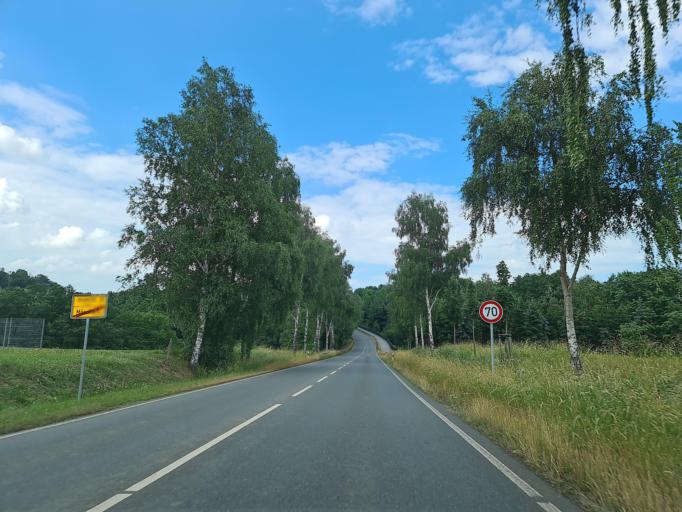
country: DE
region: Saxony
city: Pohl
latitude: 50.5323
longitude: 12.1794
